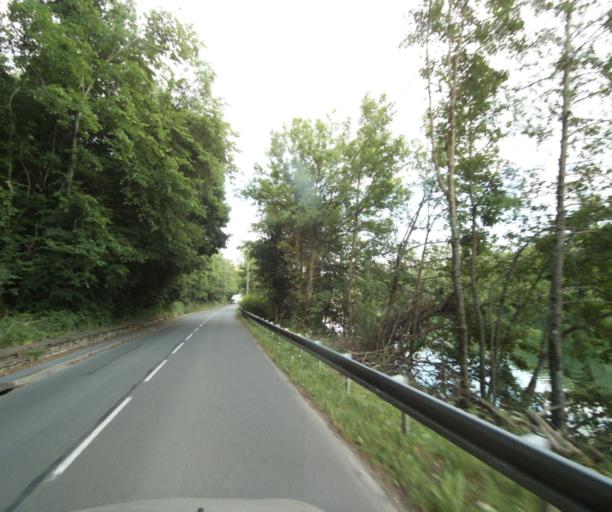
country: FR
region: Champagne-Ardenne
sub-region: Departement des Ardennes
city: Montcy-Notre-Dame
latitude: 49.7844
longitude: 4.7257
